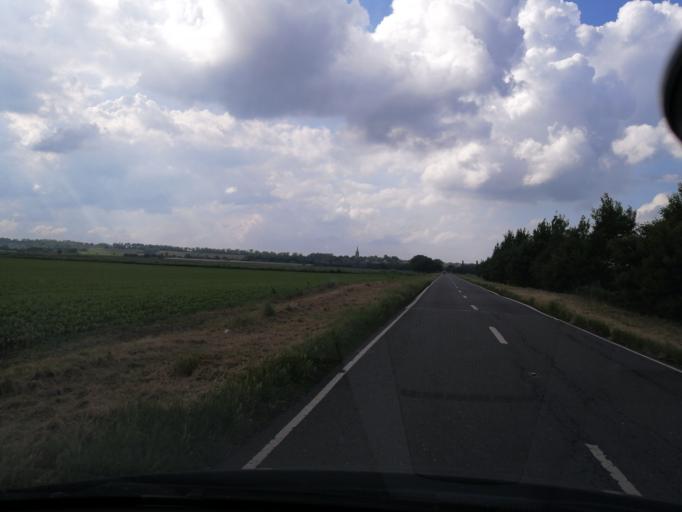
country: GB
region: England
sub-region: Cambridgeshire
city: Yaxley
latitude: 52.5021
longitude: -0.2521
